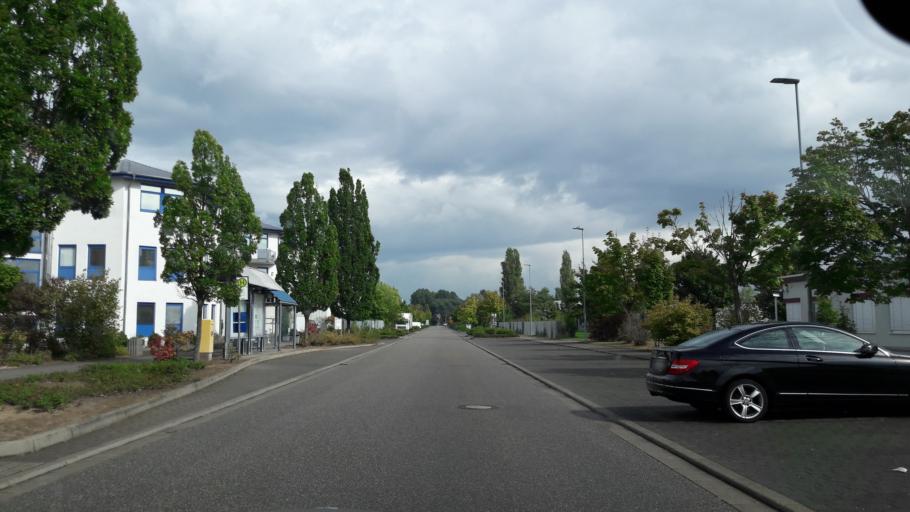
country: DE
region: Baden-Wuerttemberg
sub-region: Karlsruhe Region
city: Kronau
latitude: 49.2464
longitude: 8.6409
